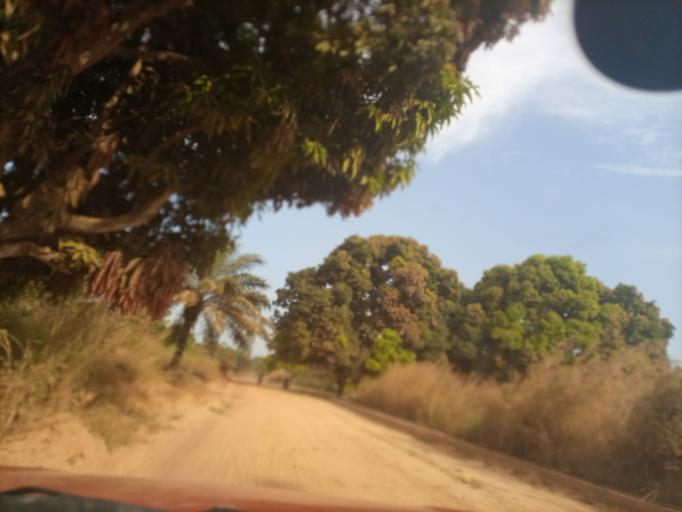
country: NG
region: Enugu
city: Obolo-Eke (1)
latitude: 6.8091
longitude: 7.5525
